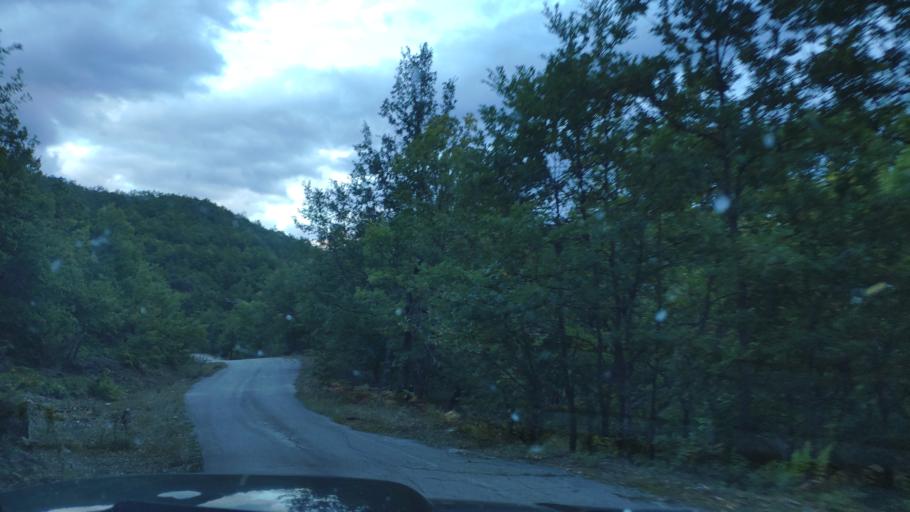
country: AL
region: Korce
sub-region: Rrethi i Kolonjes
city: Erseke
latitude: 40.2548
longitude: 20.8630
